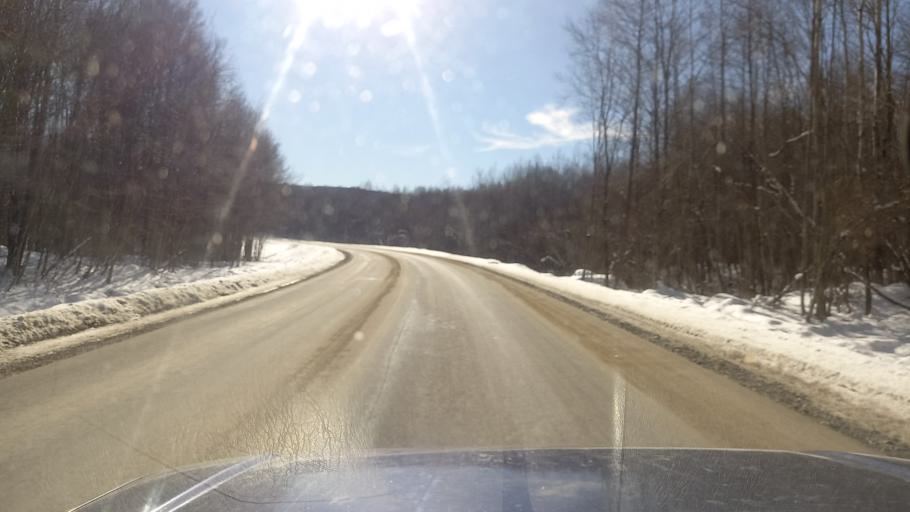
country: RU
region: Adygeya
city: Kamennomostskiy
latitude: 44.2140
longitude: 40.0766
